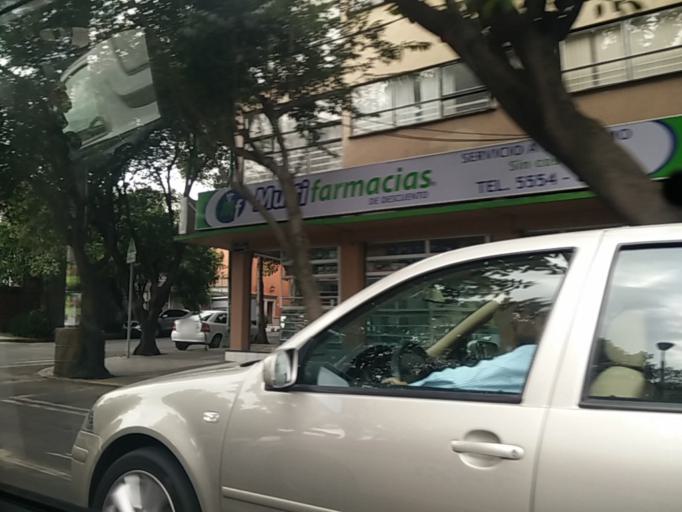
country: MX
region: Mexico City
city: Coyoacan
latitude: 19.3558
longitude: -99.1635
